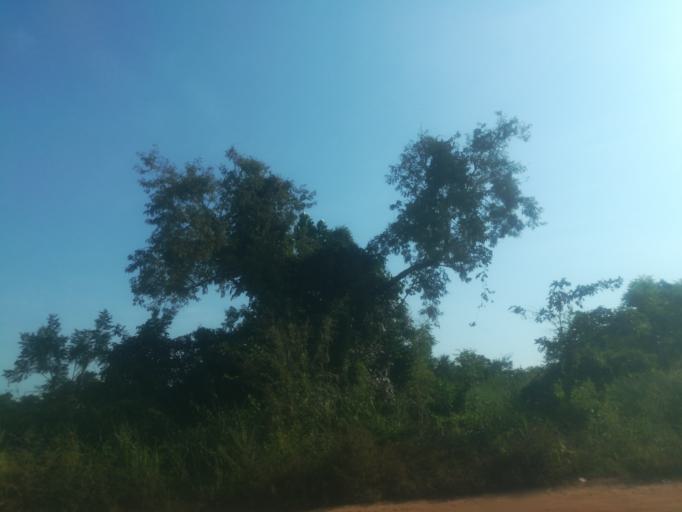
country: NG
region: Ogun
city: Abeokuta
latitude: 7.1403
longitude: 3.2570
